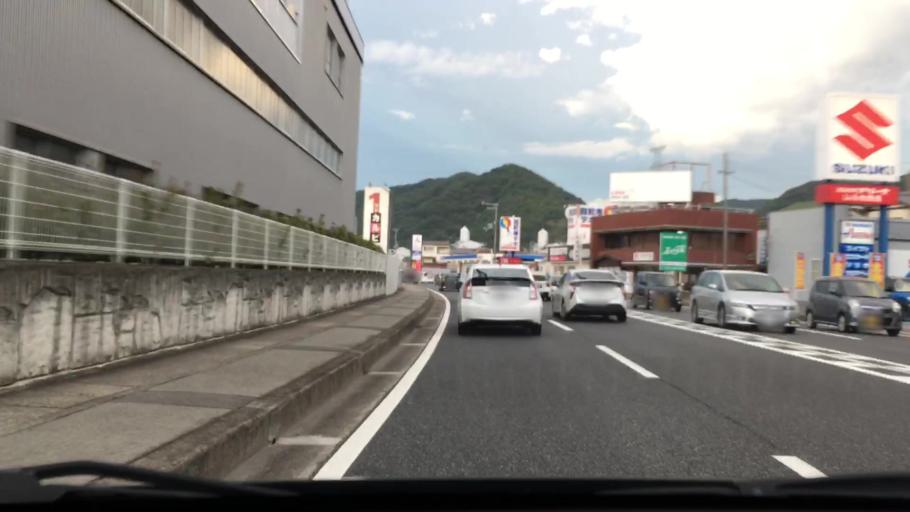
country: JP
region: Hyogo
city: Himeji
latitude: 34.8545
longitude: 134.7171
